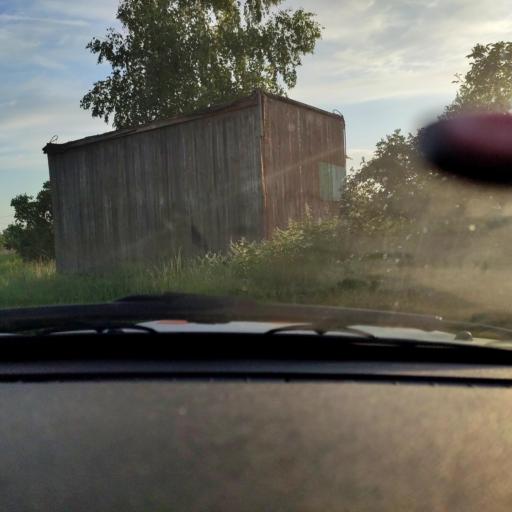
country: RU
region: Voronezj
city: Podgornoye
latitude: 51.8356
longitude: 39.1891
